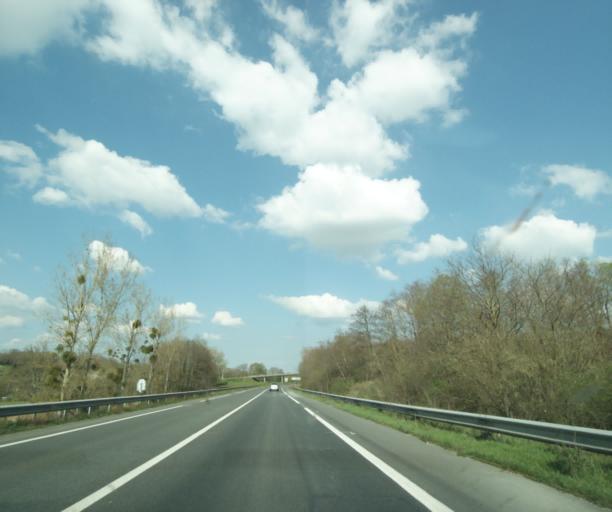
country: FR
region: Auvergne
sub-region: Departement de l'Allier
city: Bessay-sur-Allier
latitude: 46.4725
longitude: 3.3032
